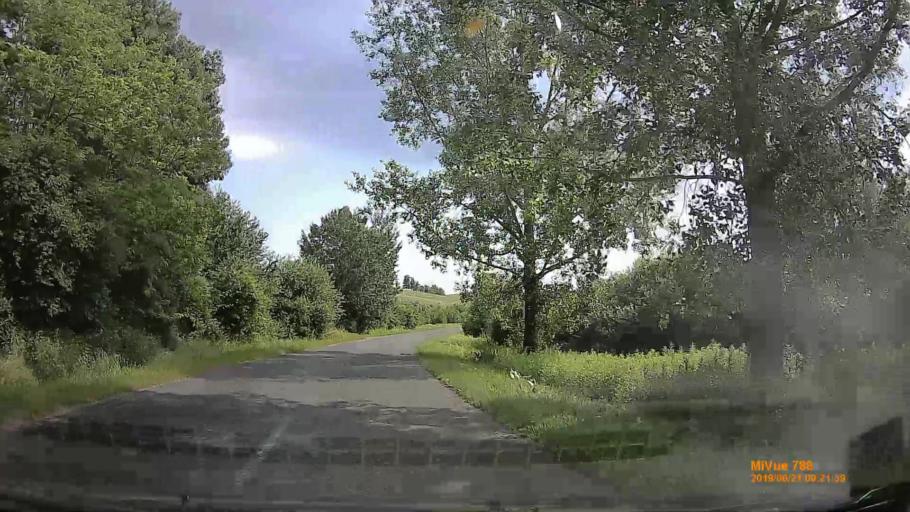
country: HU
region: Somogy
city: Taszar
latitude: 46.2425
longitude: 17.8834
